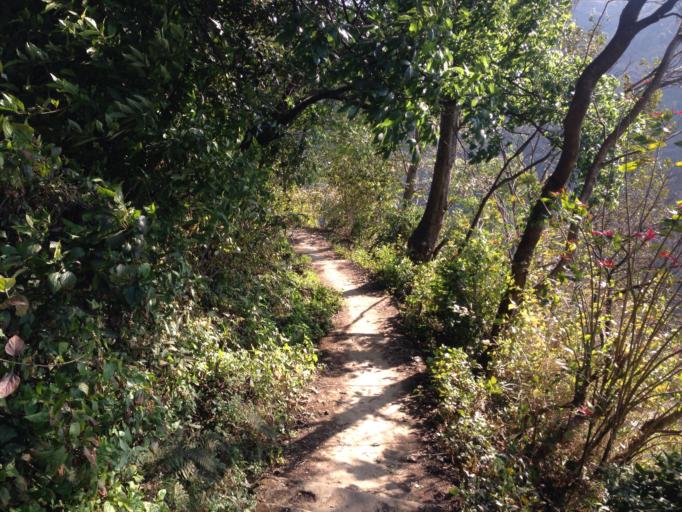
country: NP
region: Central Region
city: Kirtipur
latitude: 27.7323
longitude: 85.2643
